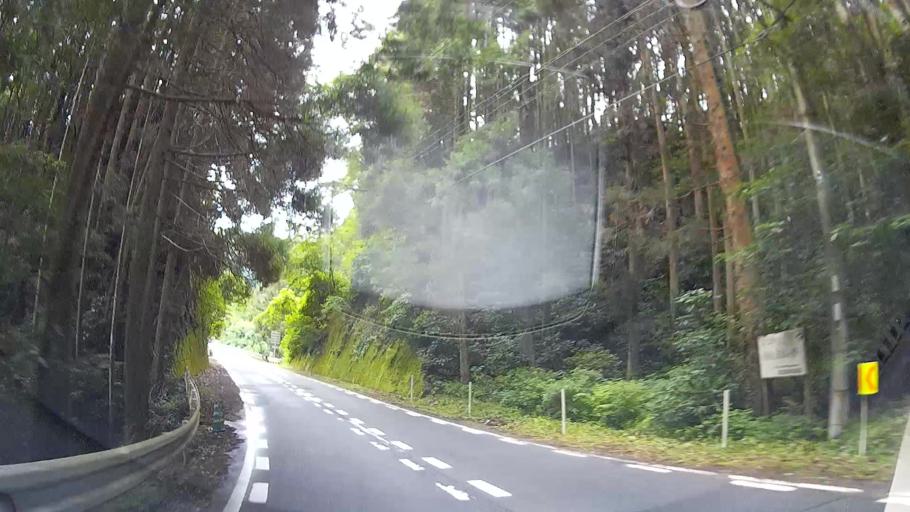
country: JP
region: Oita
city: Hita
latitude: 33.1374
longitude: 130.9798
